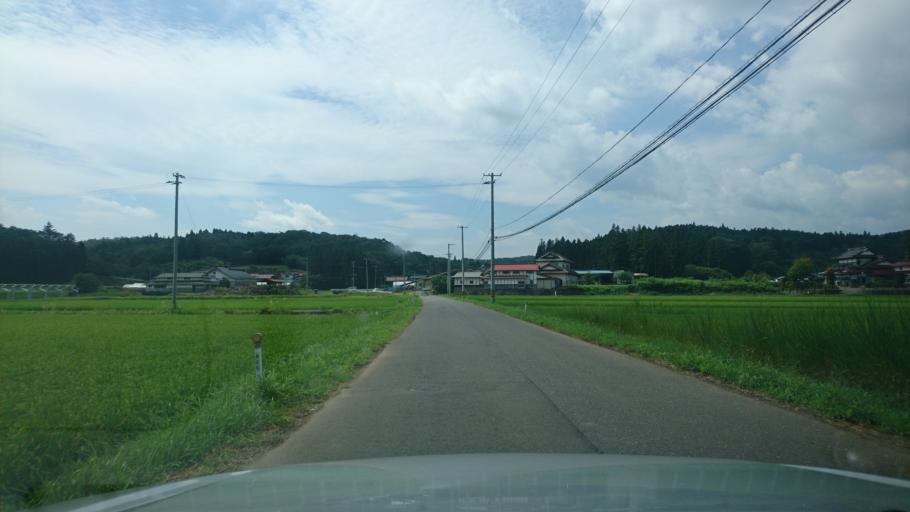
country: JP
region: Iwate
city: Ichinoseki
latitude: 38.8176
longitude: 140.9334
